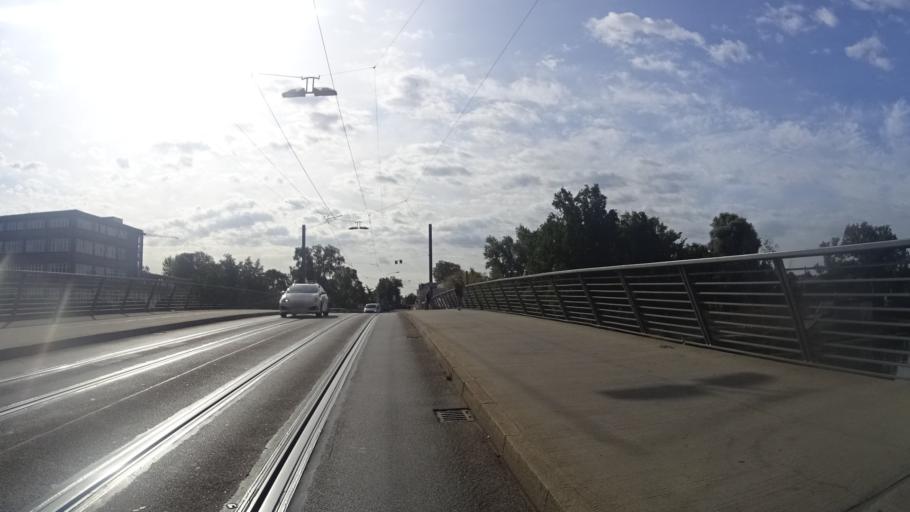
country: DE
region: Brandenburg
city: Brandenburg an der Havel
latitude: 52.4081
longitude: 12.5495
